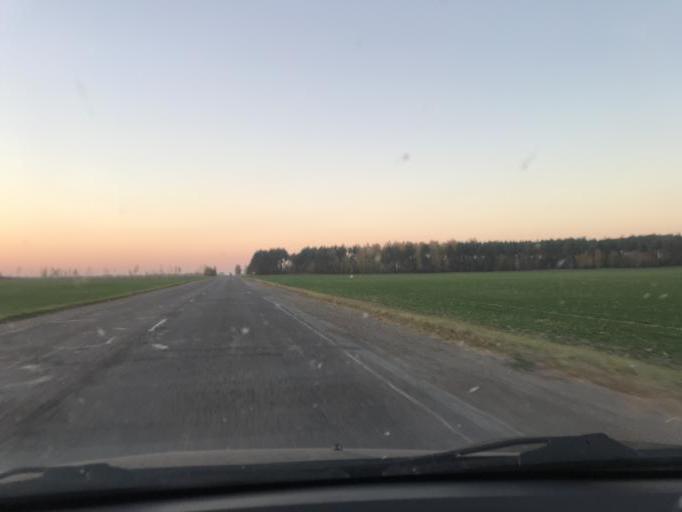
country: BY
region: Gomel
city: Horad Rechytsa
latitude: 52.1914
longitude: 30.5512
